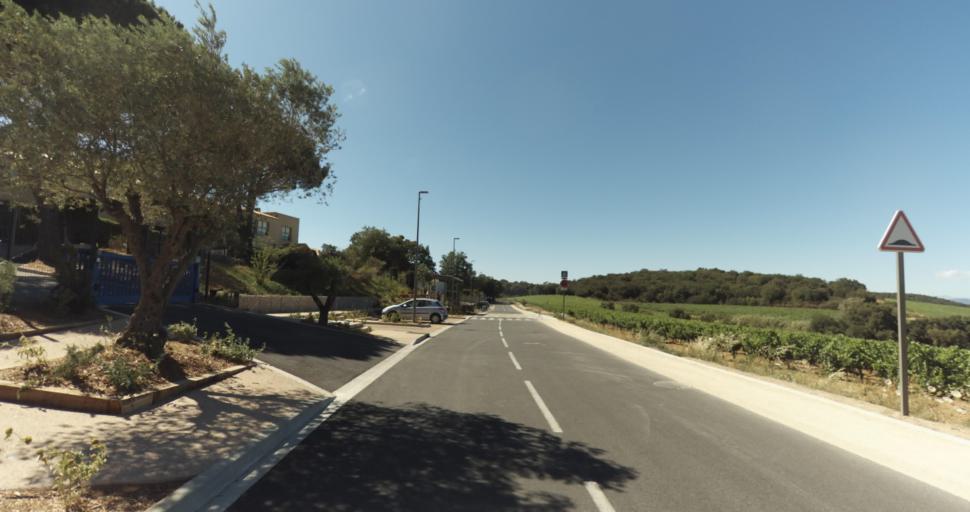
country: FR
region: Provence-Alpes-Cote d'Azur
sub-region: Departement du Var
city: La Croix-Valmer
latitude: 43.2130
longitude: 6.5617
